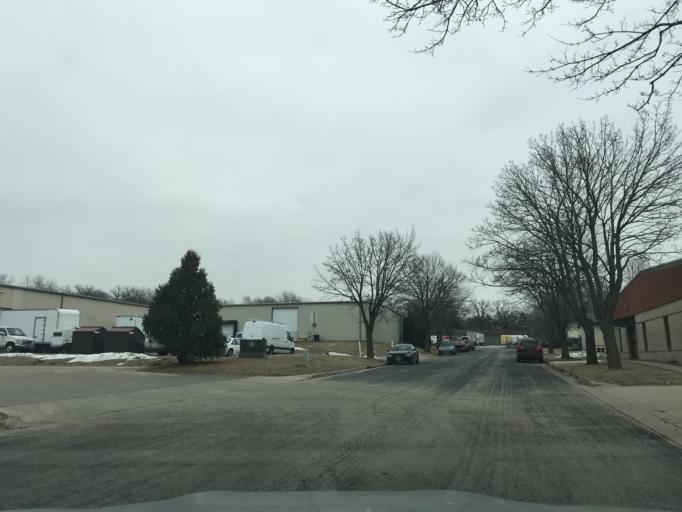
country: US
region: Wisconsin
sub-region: Dane County
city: Monona
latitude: 43.0904
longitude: -89.3094
